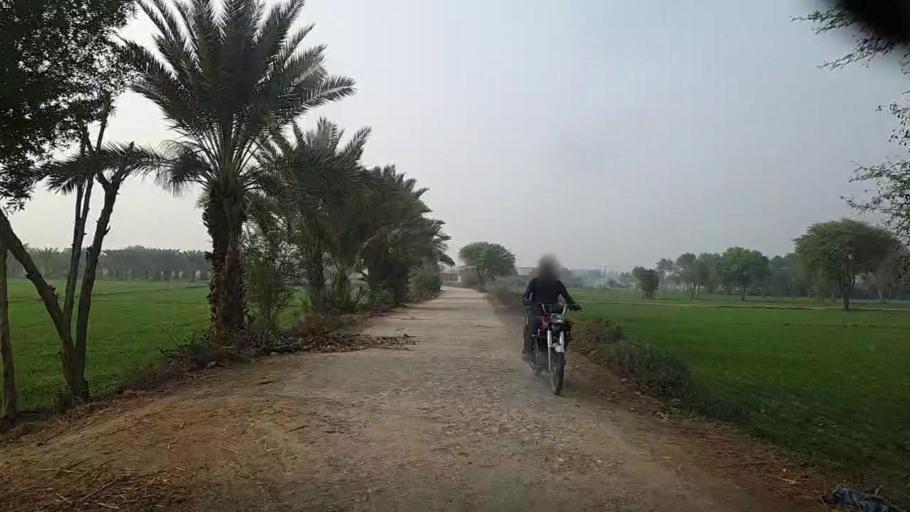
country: PK
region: Sindh
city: Bozdar
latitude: 27.1704
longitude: 68.6564
